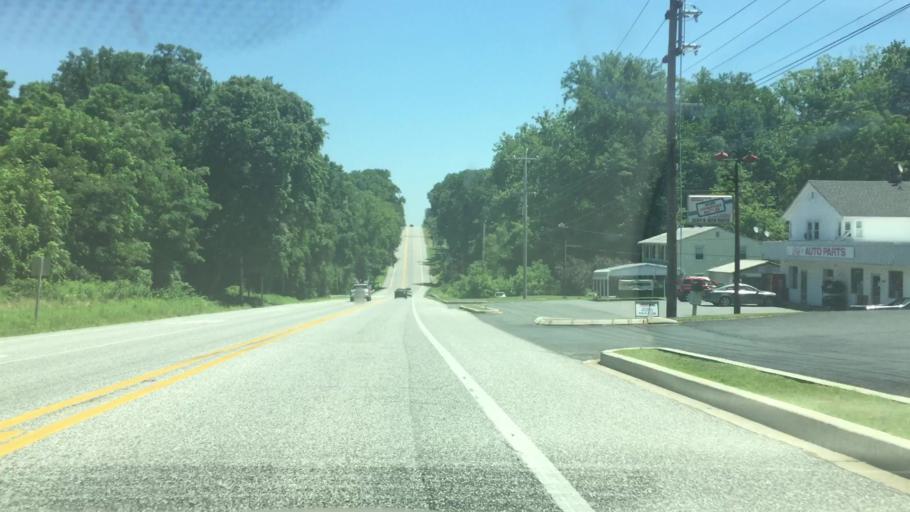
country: US
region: Maryland
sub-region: Harford County
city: Aberdeen
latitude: 39.6495
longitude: -76.1992
